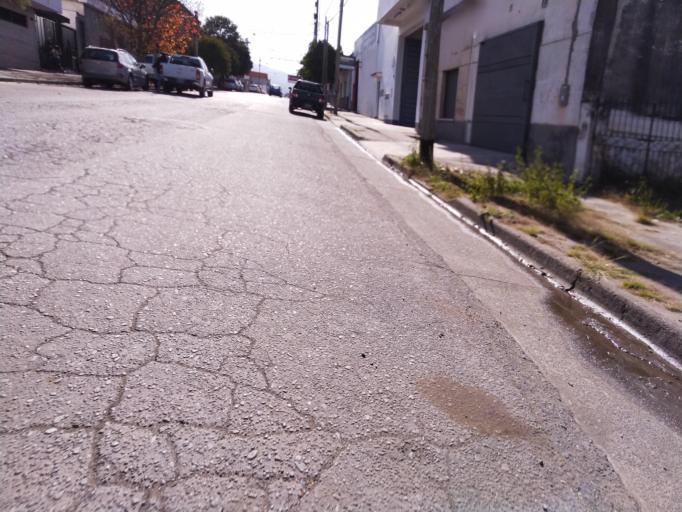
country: AR
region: Jujuy
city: San Salvador de Jujuy
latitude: -24.1988
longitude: -65.2876
